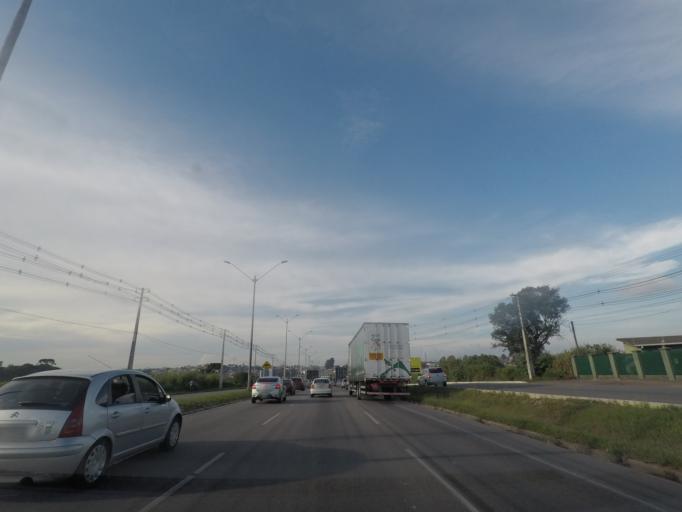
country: BR
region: Parana
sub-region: Pinhais
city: Pinhais
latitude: -25.3800
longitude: -49.1982
